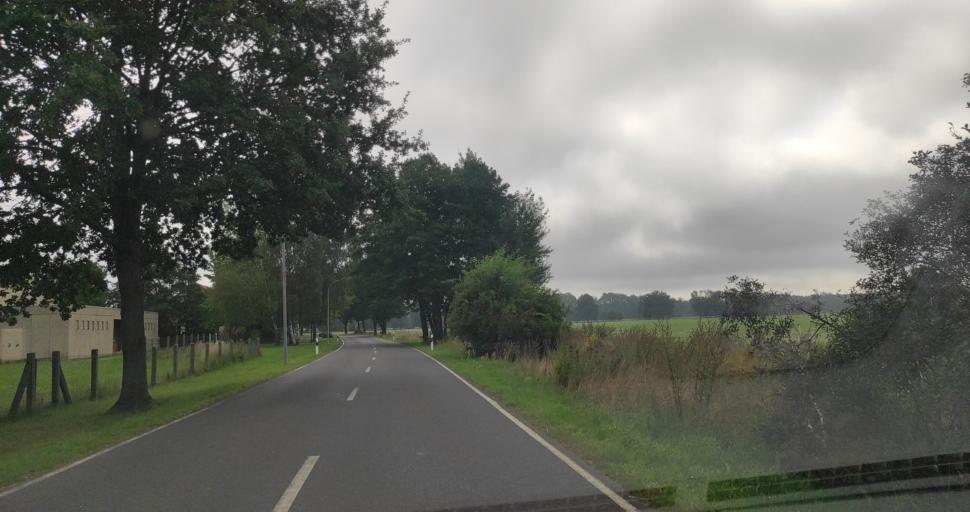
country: DE
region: Brandenburg
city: Forst
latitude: 51.6884
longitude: 14.6212
